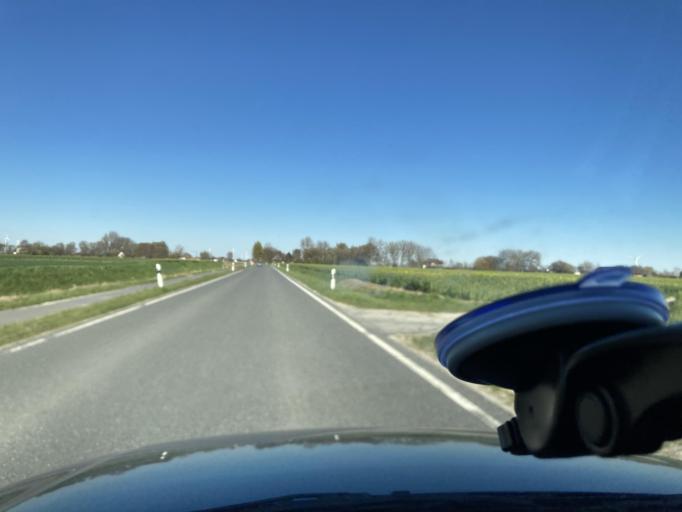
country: DE
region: Schleswig-Holstein
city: Neuenkirchen
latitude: 54.2302
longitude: 8.9651
